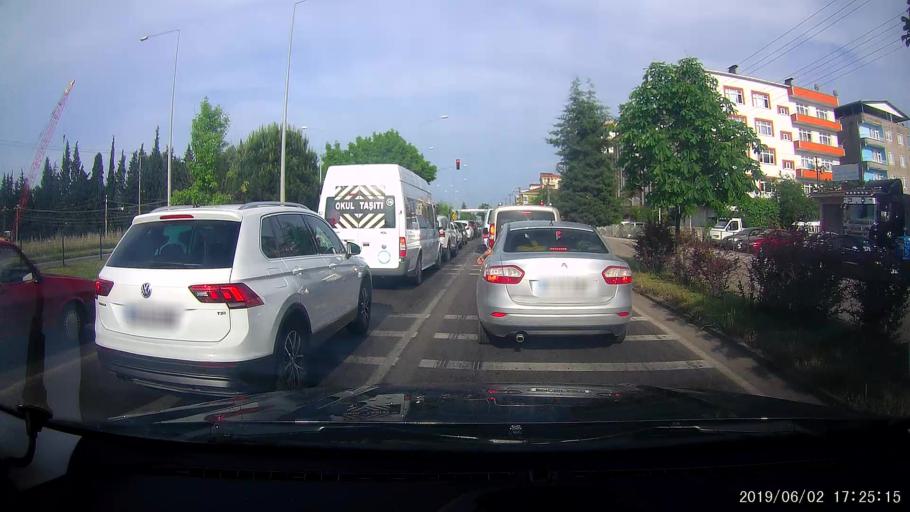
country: TR
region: Samsun
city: Carsamba
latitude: 41.2048
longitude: 36.7095
